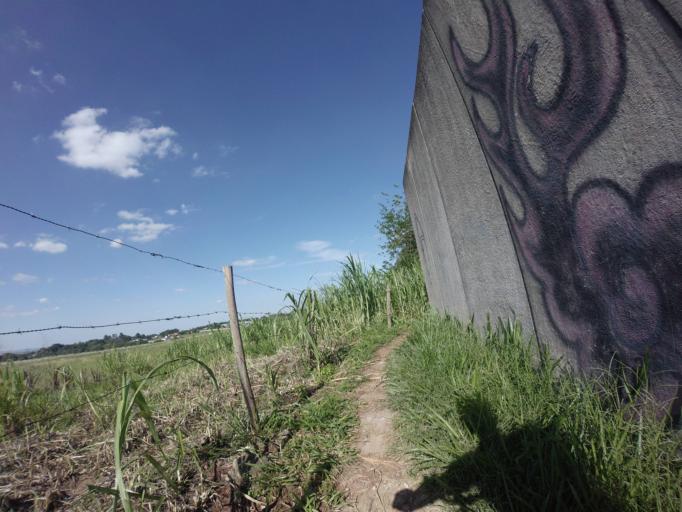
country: BR
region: Sao Paulo
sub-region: Piracicaba
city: Piracicaba
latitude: -22.7493
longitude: -47.5864
